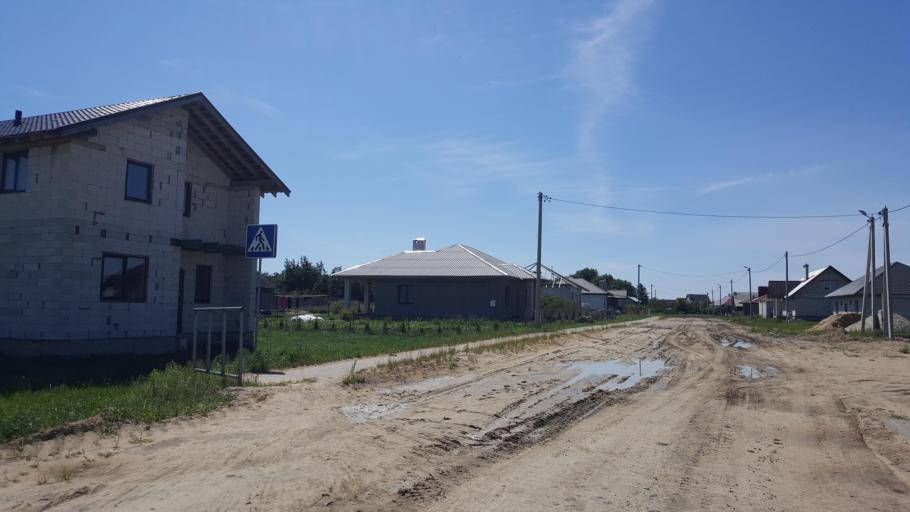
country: BY
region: Brest
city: Charnawchytsy
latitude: 52.2158
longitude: 23.7374
